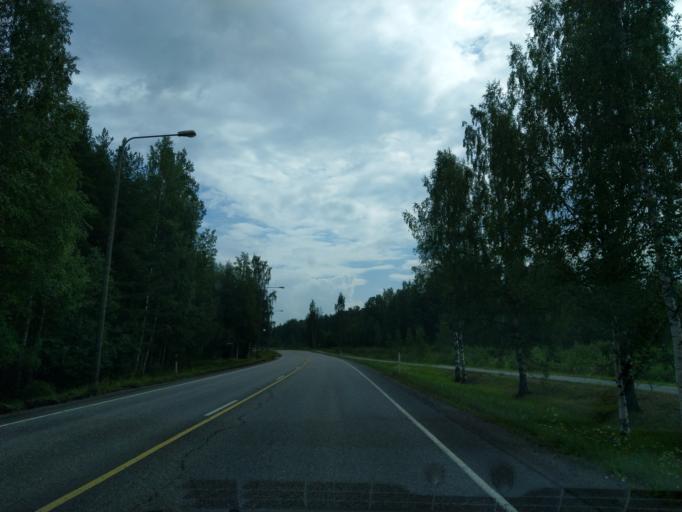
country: FI
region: South Karelia
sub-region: Imatra
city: Parikkala
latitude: 61.5961
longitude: 29.4842
